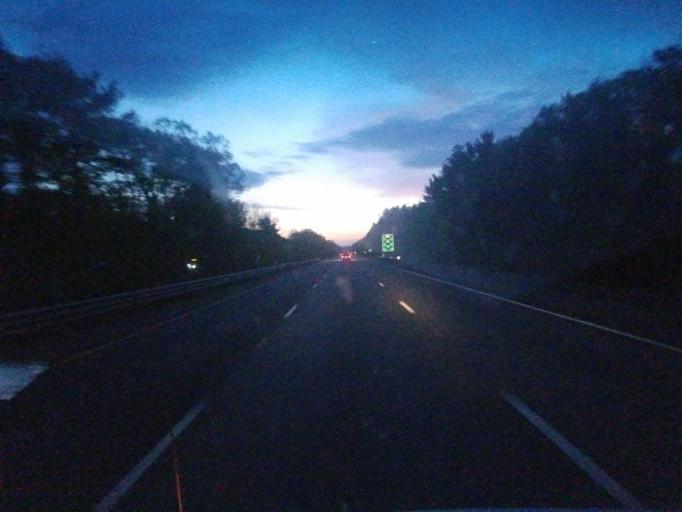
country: US
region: Massachusetts
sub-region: Worcester County
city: Bolton
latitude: 42.4539
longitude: -71.5772
